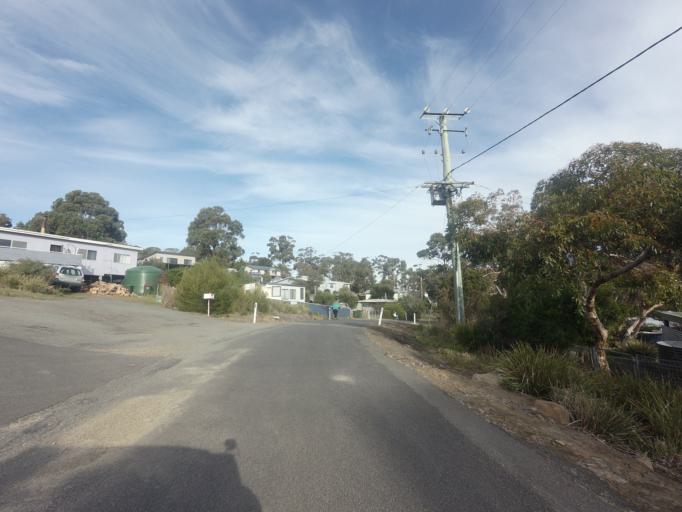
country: AU
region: Tasmania
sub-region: Sorell
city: Sorell
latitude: -42.9777
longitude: 147.8378
